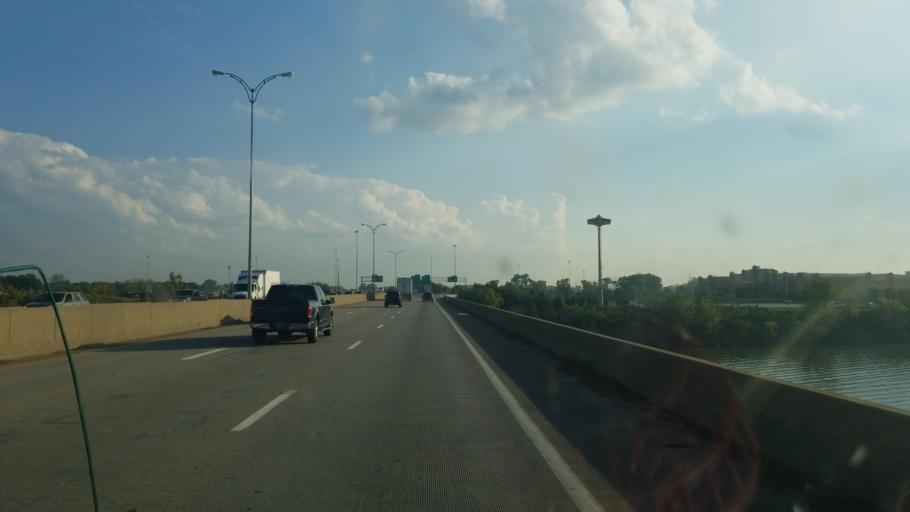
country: US
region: Ohio
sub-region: Wood County
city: Rossford
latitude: 41.6246
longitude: -83.5423
